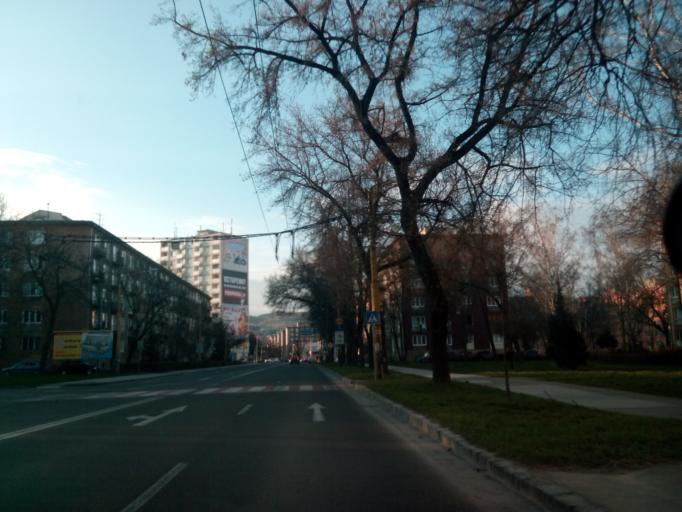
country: SK
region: Kosicky
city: Kosice
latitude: 48.7367
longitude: 21.2533
